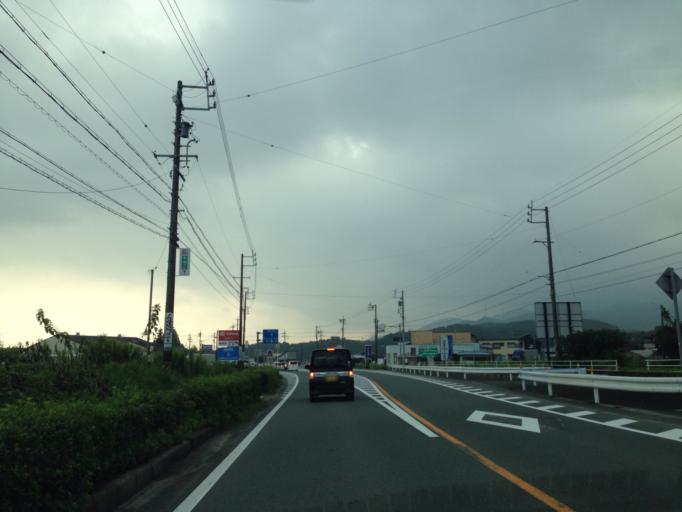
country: JP
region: Aichi
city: Shinshiro
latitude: 34.9016
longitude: 137.4842
